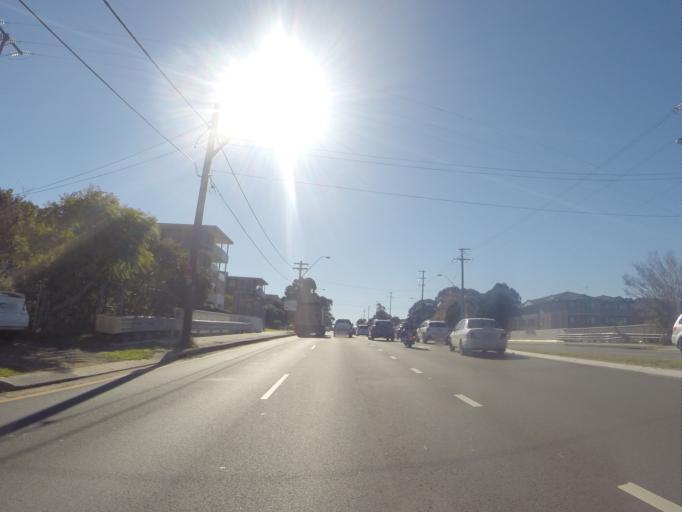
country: AU
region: New South Wales
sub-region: Sutherland Shire
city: Kirrawee
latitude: -34.0361
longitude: 151.0661
